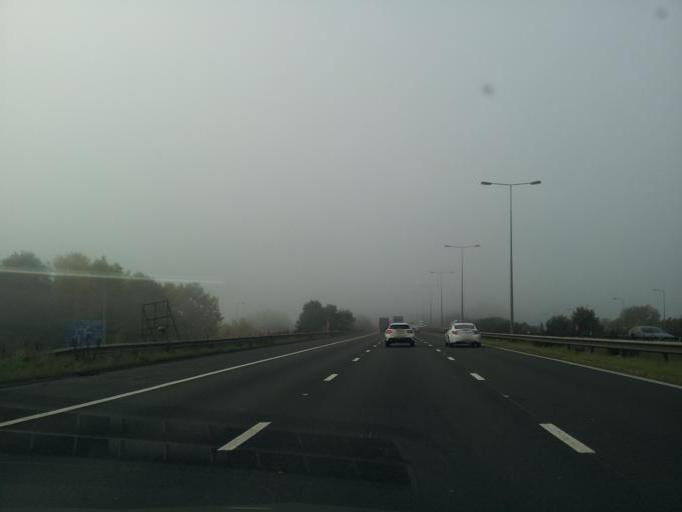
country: GB
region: England
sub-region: Kirklees
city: Cleckheaton
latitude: 53.7401
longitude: -1.7225
